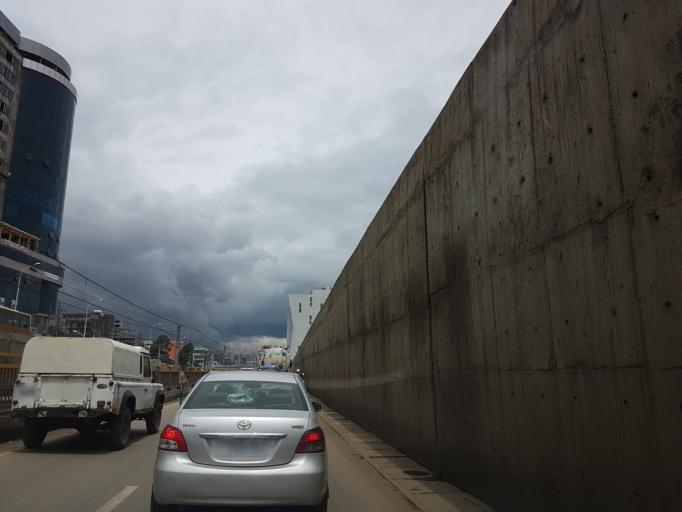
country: ET
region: Adis Abeba
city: Addis Ababa
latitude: 9.0187
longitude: 38.8001
